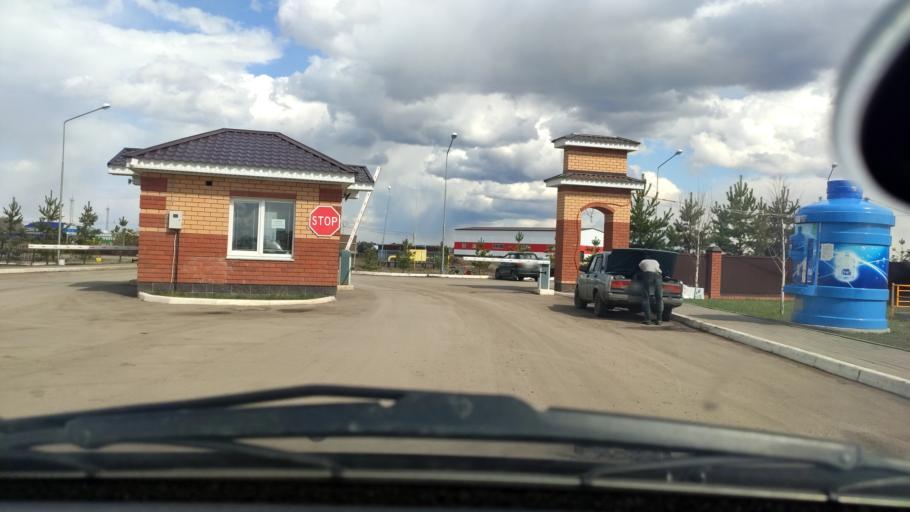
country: RU
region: Bashkortostan
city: Ufa
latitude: 54.6215
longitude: 55.8868
